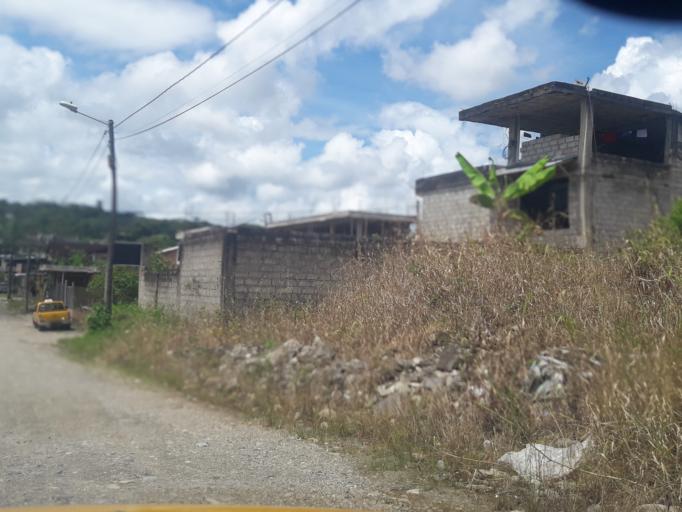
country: EC
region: Napo
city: Tena
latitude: -1.0089
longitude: -77.8165
